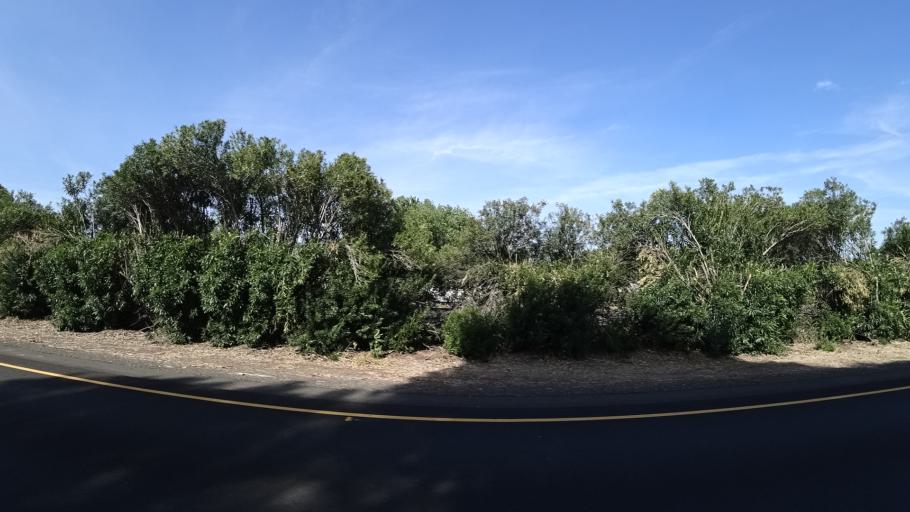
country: US
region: California
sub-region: Butte County
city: Chico
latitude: 39.7685
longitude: -121.8662
